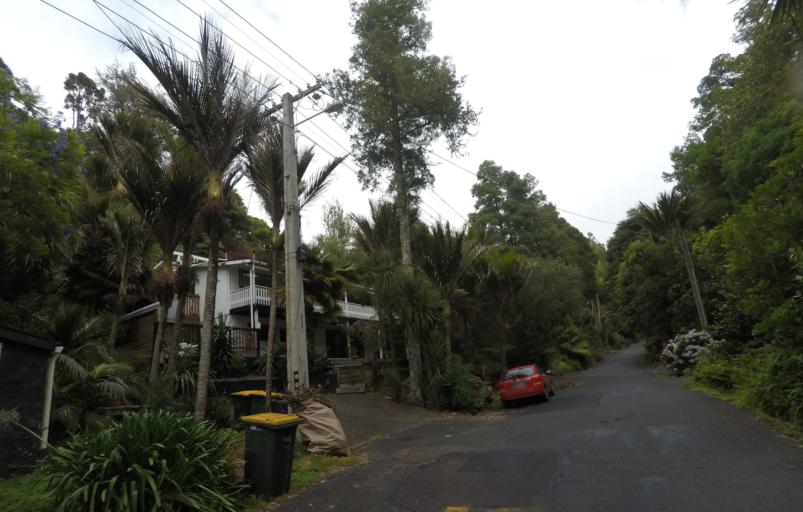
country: NZ
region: Auckland
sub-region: Auckland
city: Titirangi
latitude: -36.9476
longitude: 174.6629
